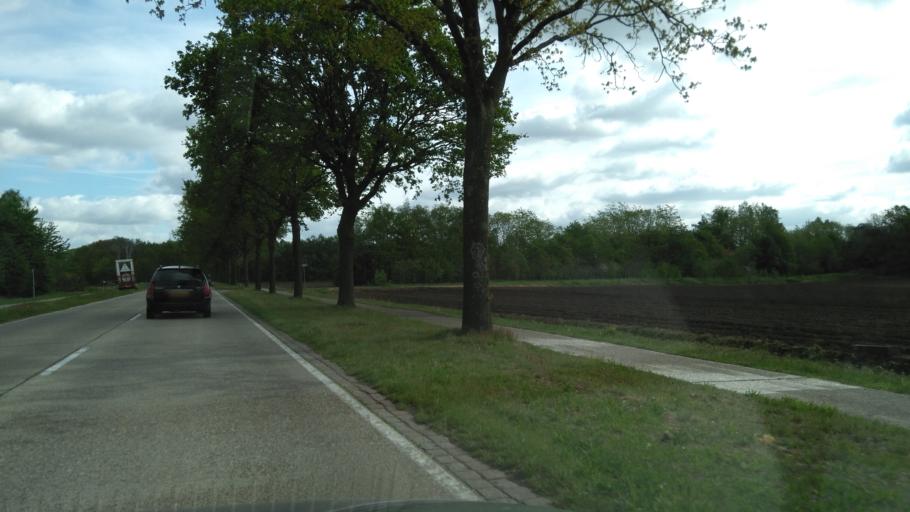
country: NL
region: North Brabant
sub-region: Gemeente Baarle-Nassau
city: Baarle-Nassau
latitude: 51.5072
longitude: 4.9826
